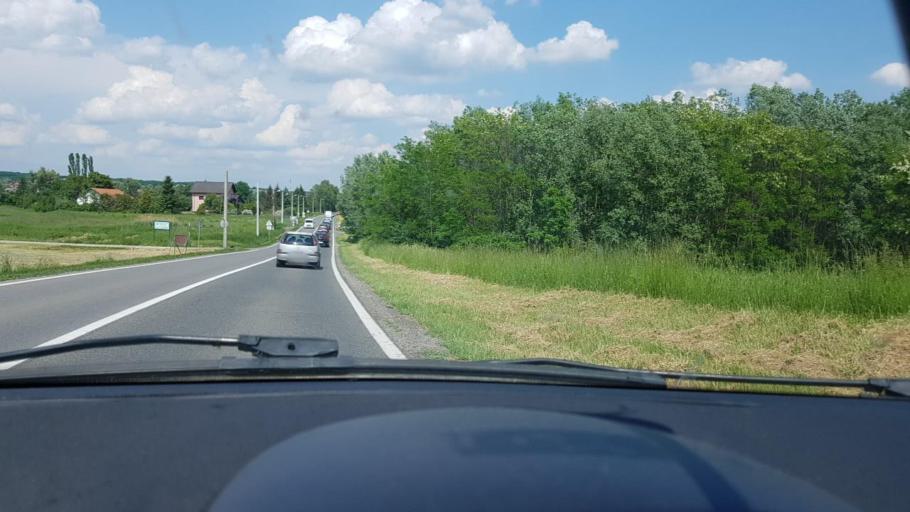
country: HR
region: Grad Zagreb
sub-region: Sesvete
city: Sesvete
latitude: 45.8778
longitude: 16.1671
